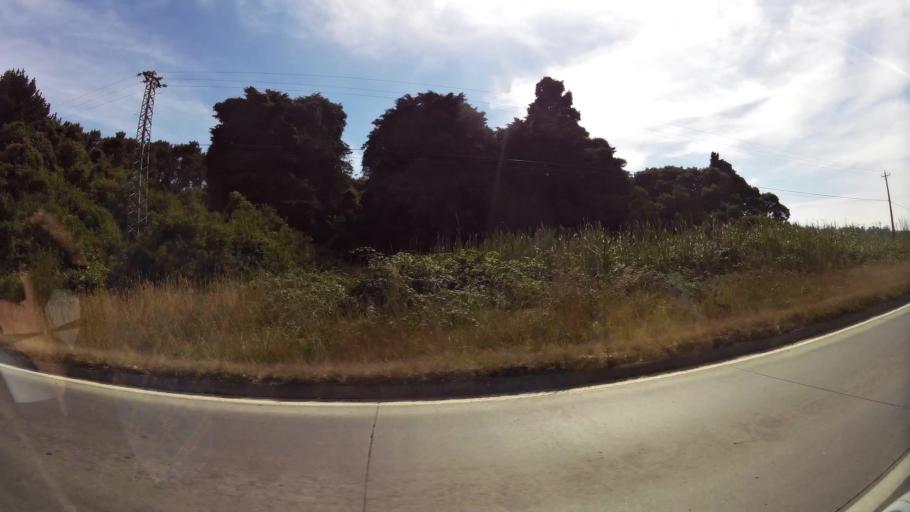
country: CL
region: Biobio
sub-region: Provincia de Concepcion
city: Talcahuano
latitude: -36.7582
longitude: -73.1216
